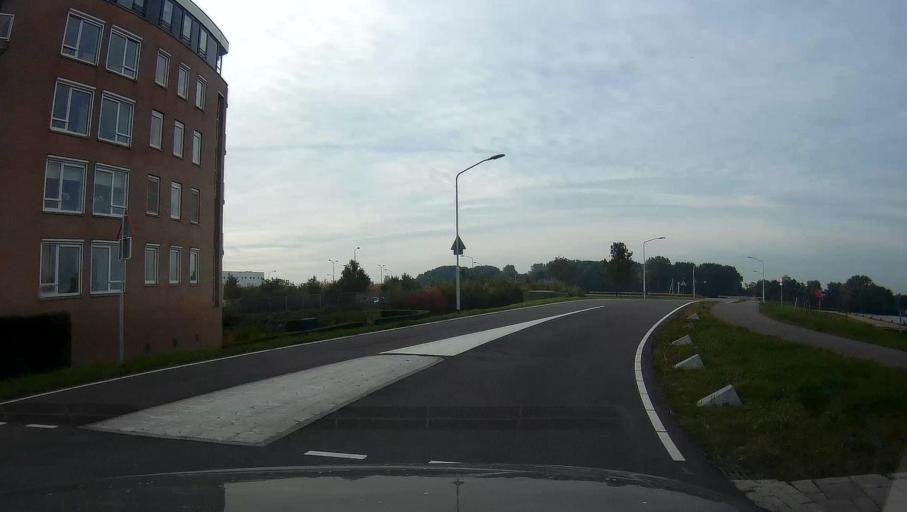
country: NL
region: South Holland
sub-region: Gemeente Papendrecht
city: Papendrecht
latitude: 51.8305
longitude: 4.6729
